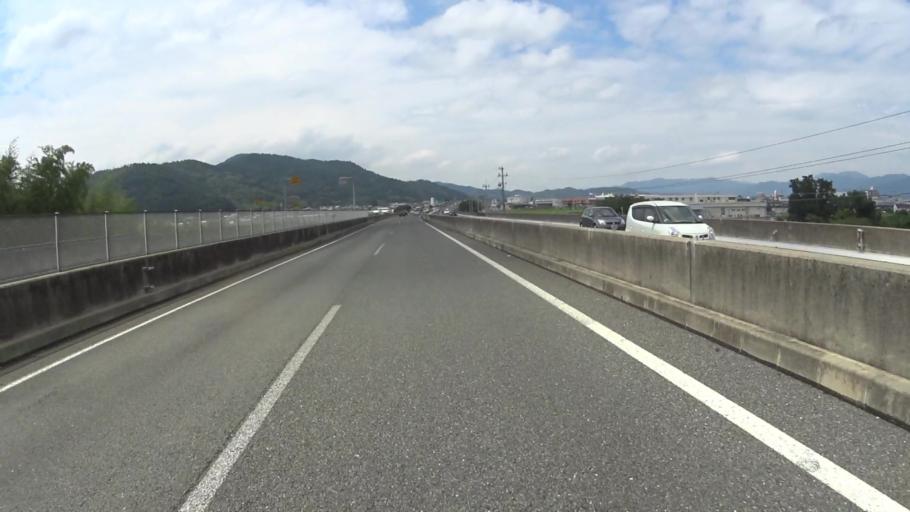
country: JP
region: Kyoto
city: Kameoka
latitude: 35.0216
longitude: 135.5508
